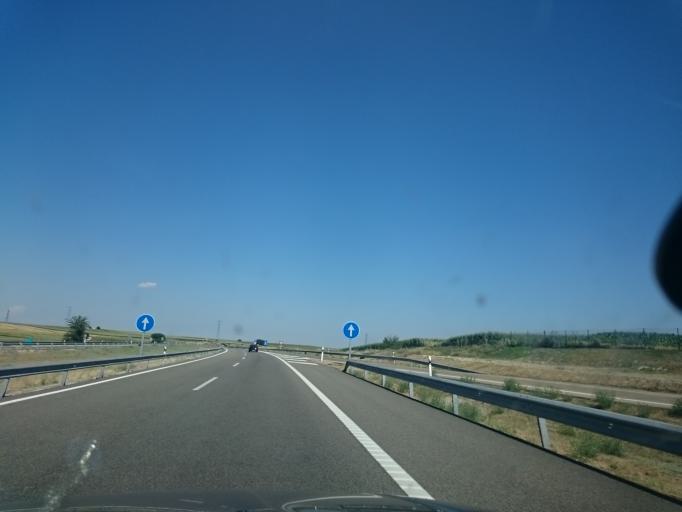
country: ES
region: Aragon
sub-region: Provincia de Huesca
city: Valfarta
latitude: 41.5176
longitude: -0.0964
